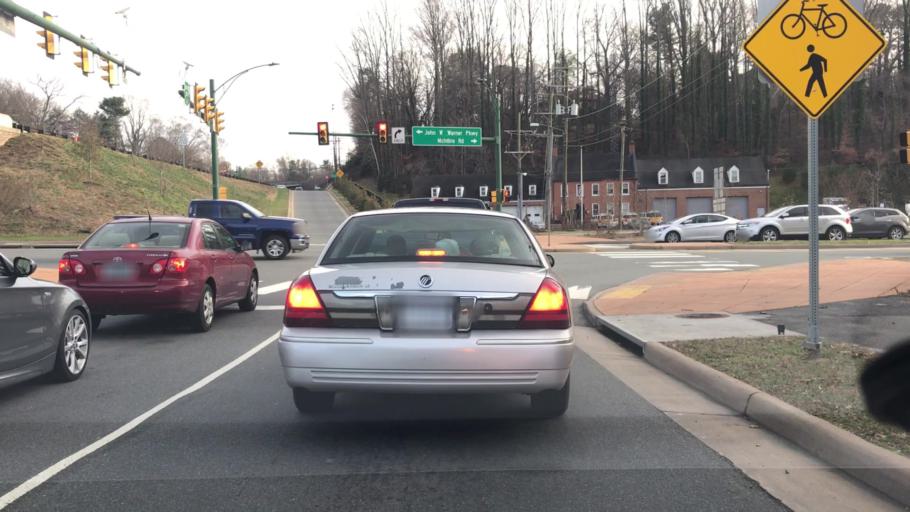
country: US
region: Virginia
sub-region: City of Charlottesville
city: Charlottesville
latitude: 38.0427
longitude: -78.4754
